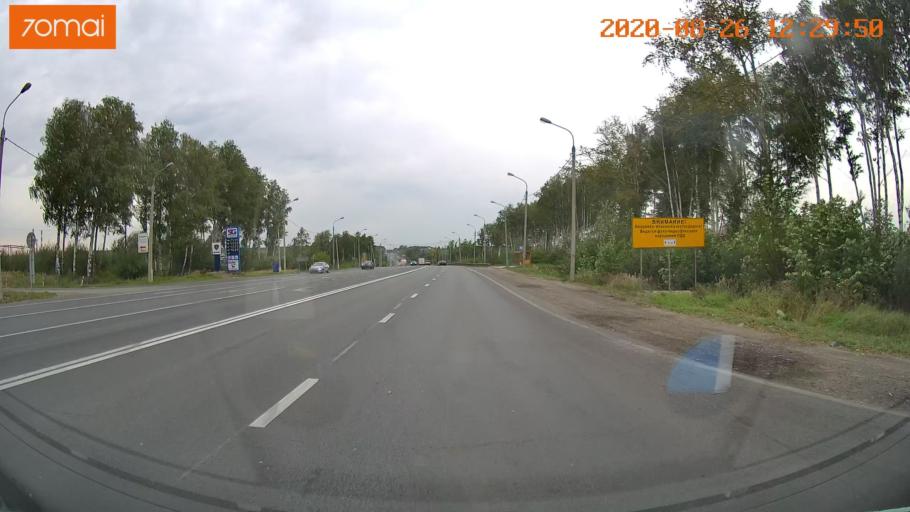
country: RU
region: Rjazan
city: Ryazan'
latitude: 54.5664
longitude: 39.8121
